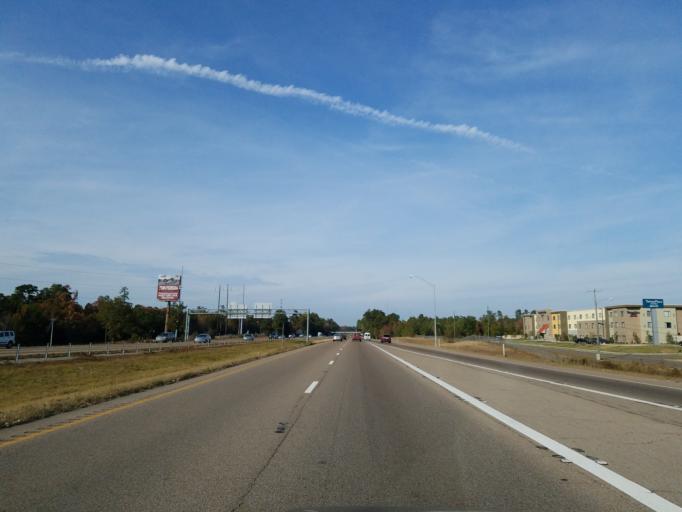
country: US
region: Mississippi
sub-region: Lamar County
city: Arnold Line
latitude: 31.3296
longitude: -89.3522
